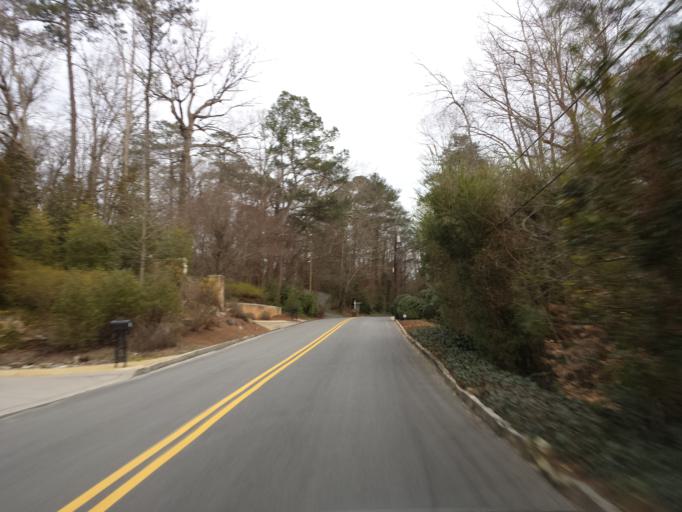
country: US
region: Georgia
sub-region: Cobb County
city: Vinings
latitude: 33.8850
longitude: -84.4234
